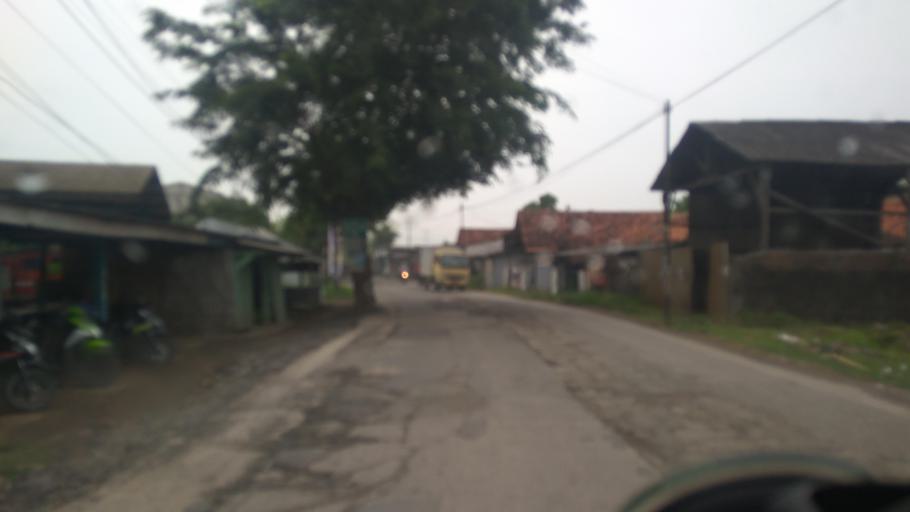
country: ID
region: West Java
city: Bekasi
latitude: -6.2041
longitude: 107.0342
